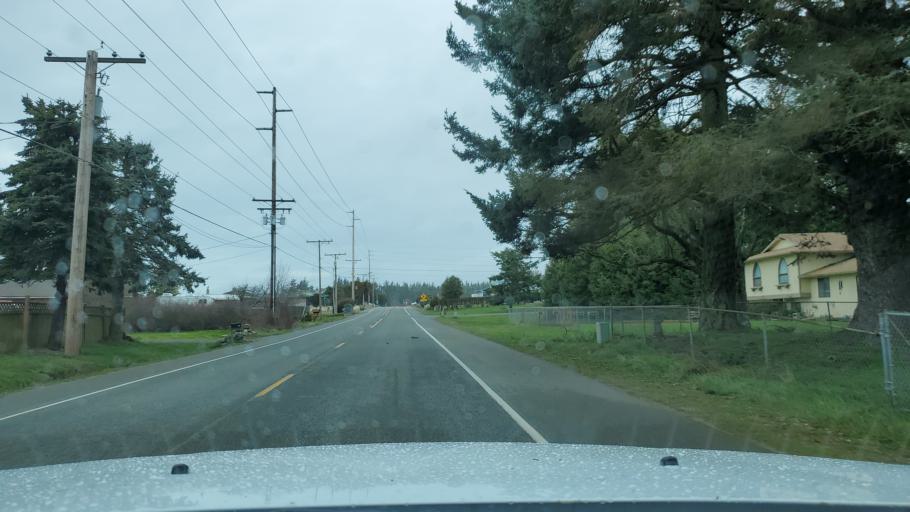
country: US
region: Washington
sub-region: Island County
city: Coupeville
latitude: 48.2806
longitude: -122.7296
